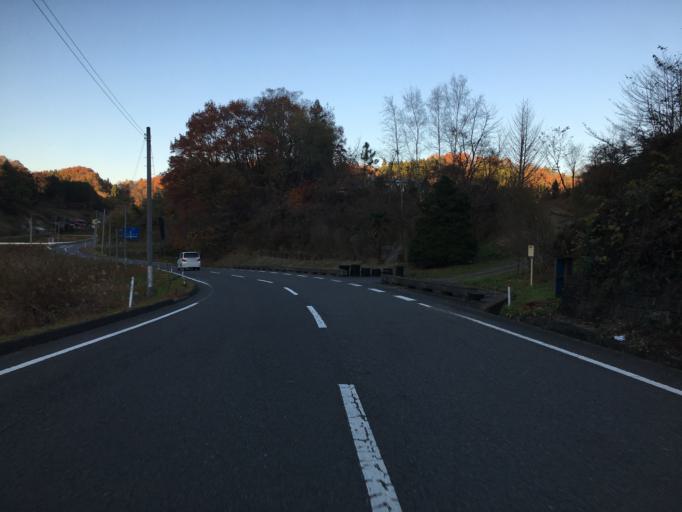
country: JP
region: Fukushima
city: Motomiya
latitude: 37.5259
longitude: 140.4603
